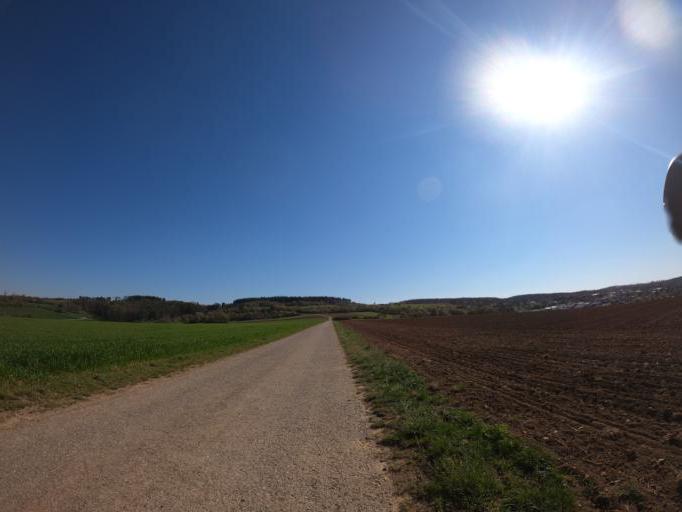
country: DE
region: Baden-Wuerttemberg
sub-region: Karlsruhe Region
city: Wiernsheim
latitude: 48.8900
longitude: 8.8650
